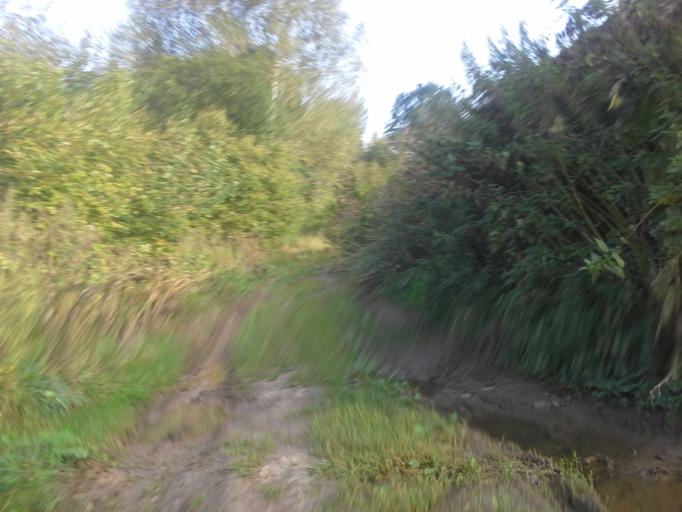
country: RU
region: Moskovskaya
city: Filimonki
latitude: 55.5479
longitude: 37.3367
